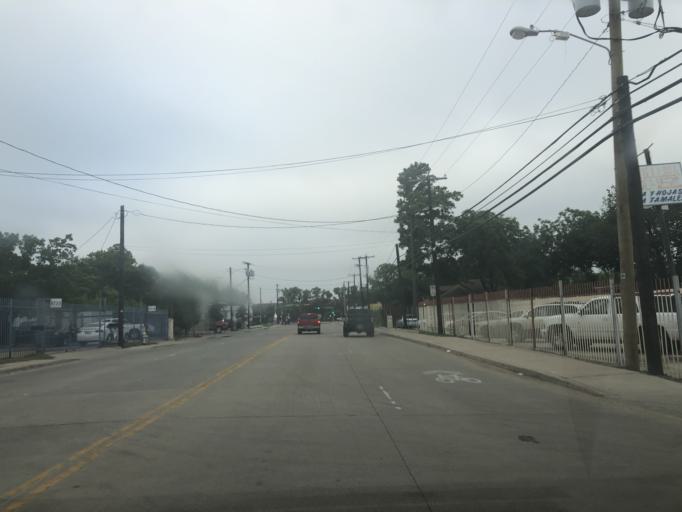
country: US
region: Texas
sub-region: Dallas County
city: Farmers Branch
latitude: 32.8682
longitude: -96.8754
